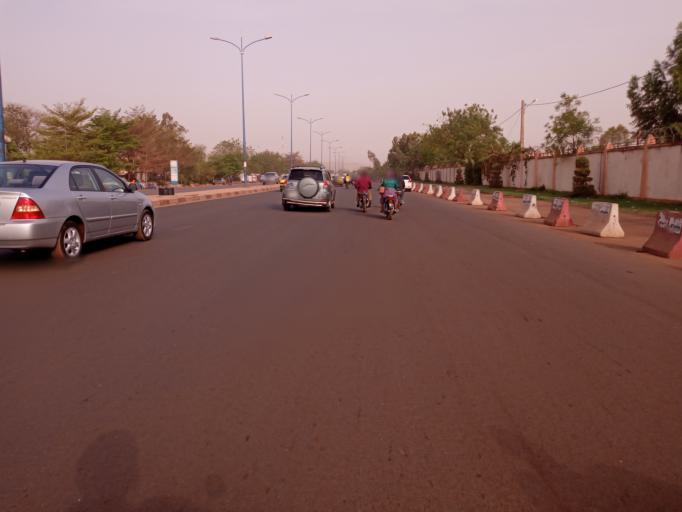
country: ML
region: Bamako
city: Bamako
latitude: 12.6340
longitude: -8.0132
